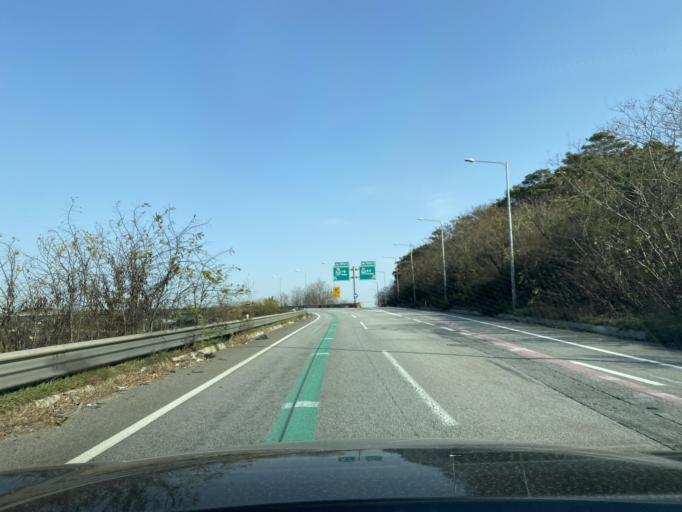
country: KR
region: Gyeonggi-do
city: Hwaseong-si
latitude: 37.0514
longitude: 126.8884
